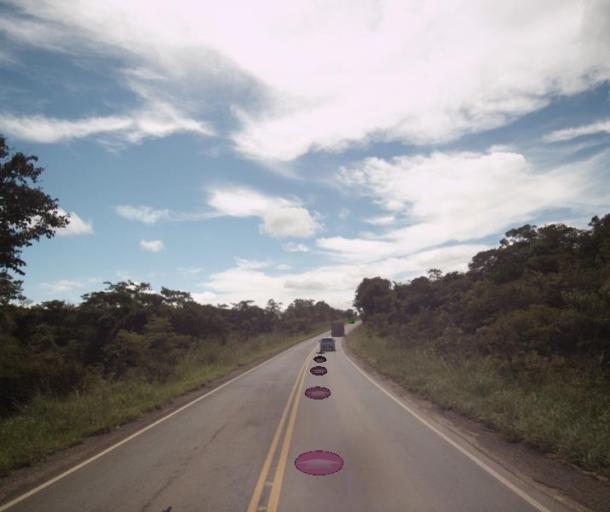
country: BR
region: Goias
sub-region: Padre Bernardo
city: Padre Bernardo
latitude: -15.4587
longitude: -48.2164
